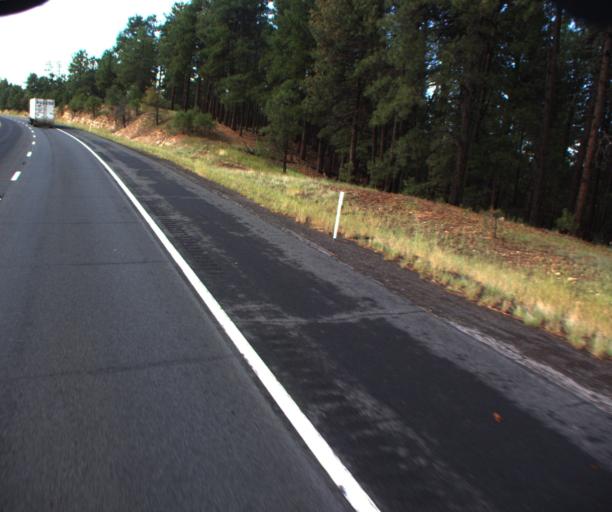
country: US
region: Arizona
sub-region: Coconino County
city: Kachina Village
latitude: 35.1286
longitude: -111.6845
